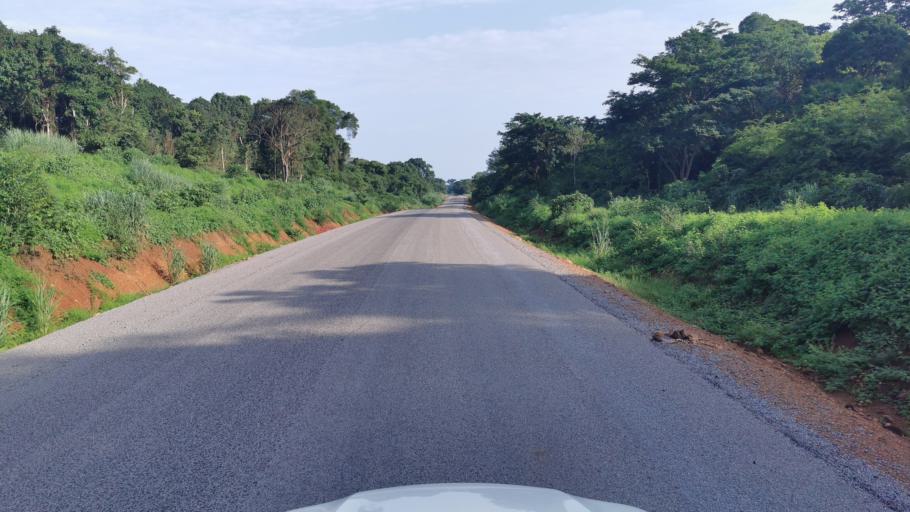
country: ET
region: Gambela
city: Gambela
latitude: 7.7384
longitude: 34.6618
